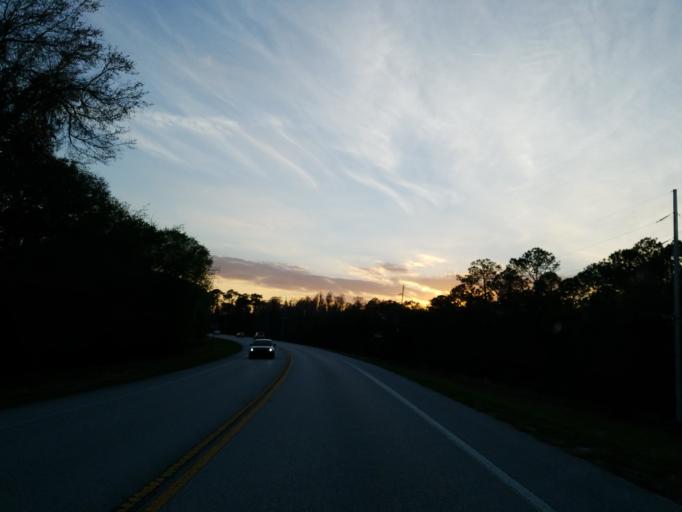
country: US
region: Florida
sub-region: Hillsborough County
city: Thonotosassa
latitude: 28.0795
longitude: -82.3391
